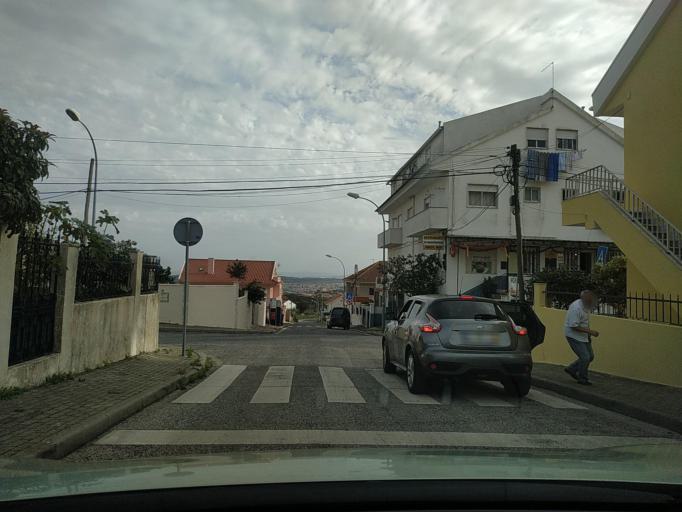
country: PT
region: Lisbon
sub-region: Sintra
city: Belas
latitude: 38.7782
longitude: -9.2435
